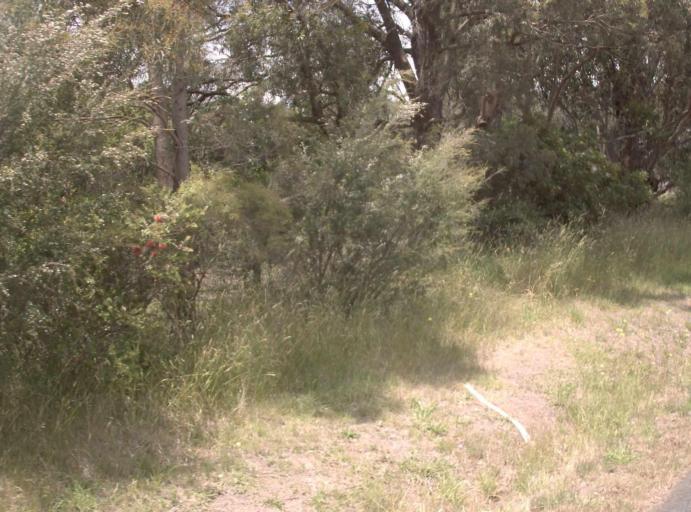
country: AU
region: Victoria
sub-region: Latrobe
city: Traralgon
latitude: -38.3283
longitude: 146.7238
